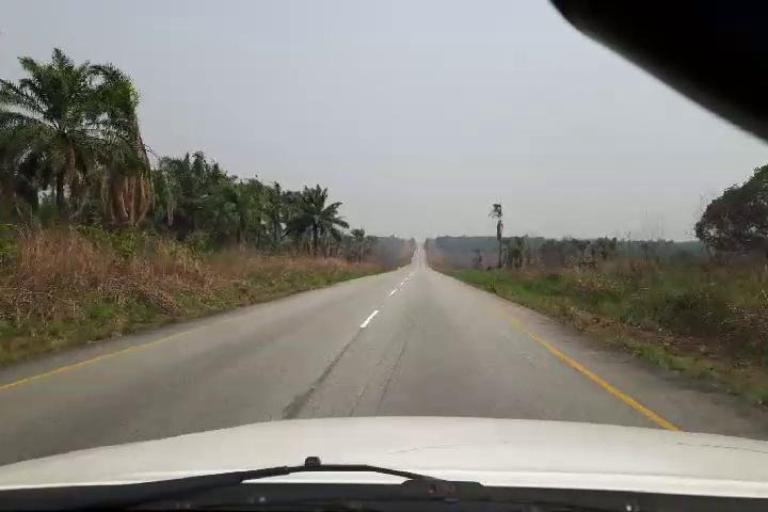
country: SL
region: Southern Province
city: Largo
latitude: 8.2356
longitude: -12.0823
